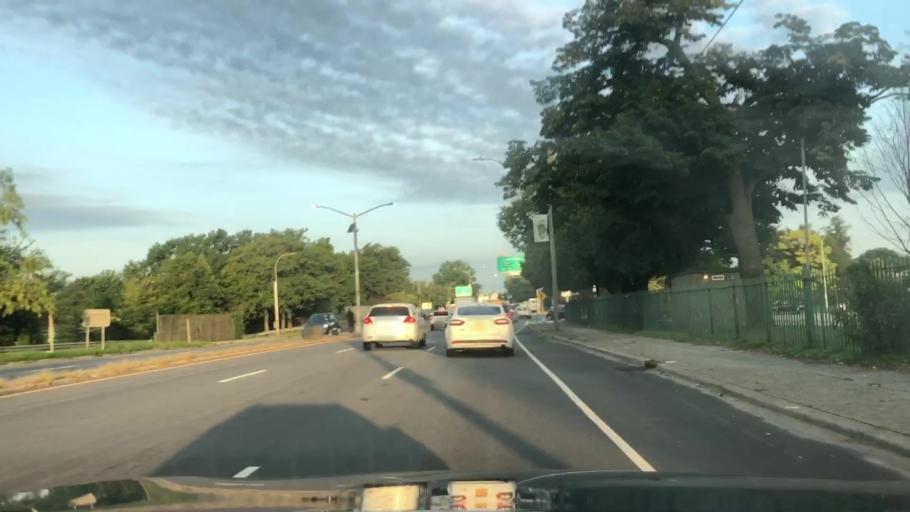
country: US
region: New York
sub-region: Nassau County
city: Bellerose Terrace
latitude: 40.7107
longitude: -73.7265
